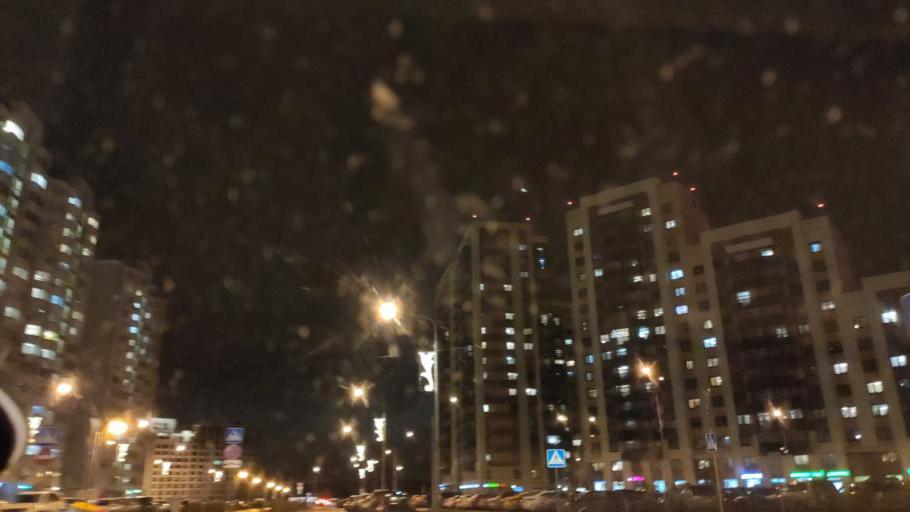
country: RU
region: Moscow
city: Novo-Peredelkino
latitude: 55.6393
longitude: 37.3283
